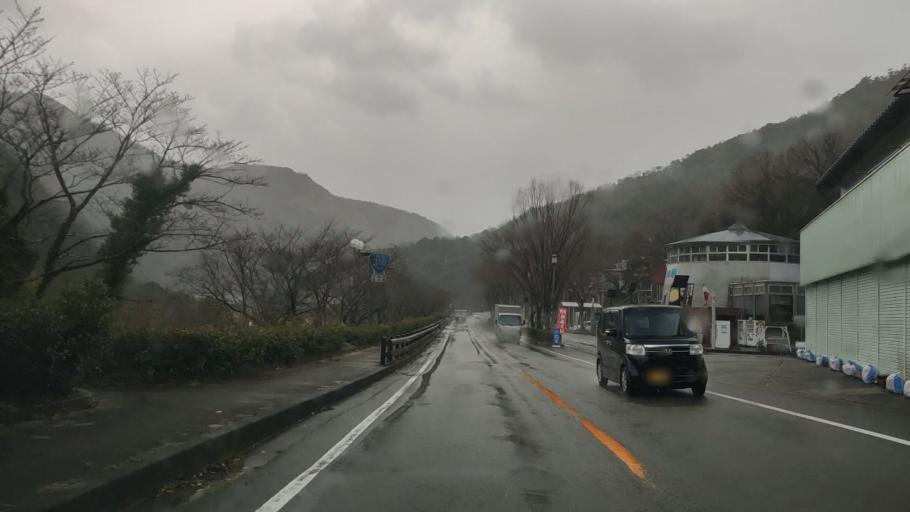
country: JP
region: Tokushima
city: Kamojimacho-jogejima
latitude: 34.1516
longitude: 134.3526
